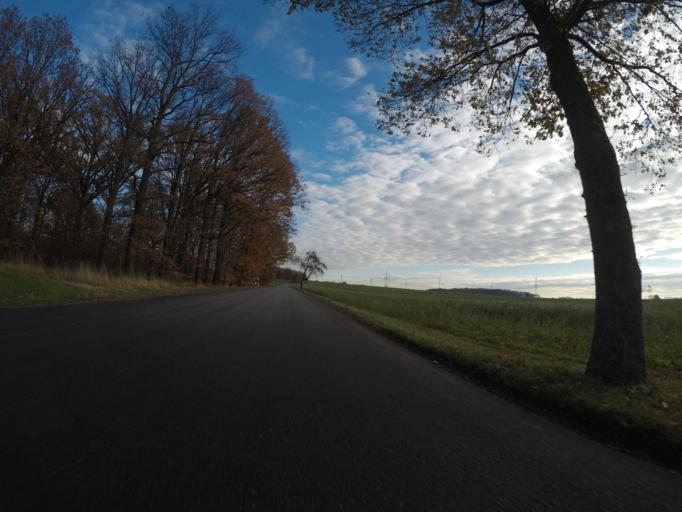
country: DE
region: Thuringia
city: Vollmershain
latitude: 50.8536
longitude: 12.3179
